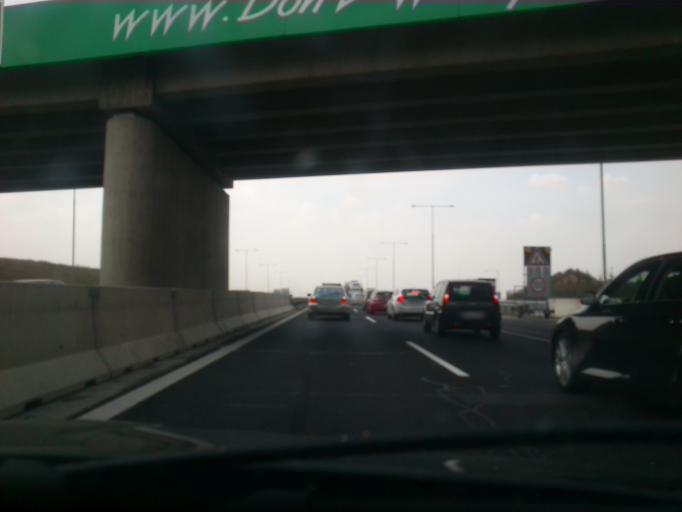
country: CZ
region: Central Bohemia
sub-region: Okres Praha-Vychod
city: Ricany
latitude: 49.9730
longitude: 14.6158
